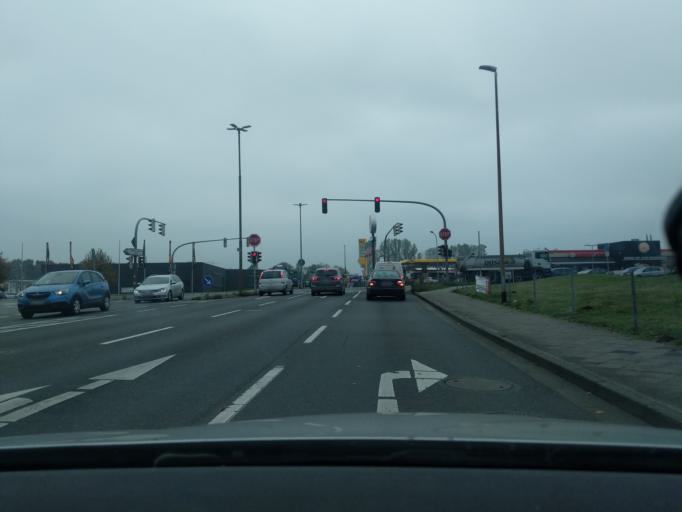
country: DE
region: Lower Saxony
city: Stade
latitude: 53.5952
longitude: 9.4232
